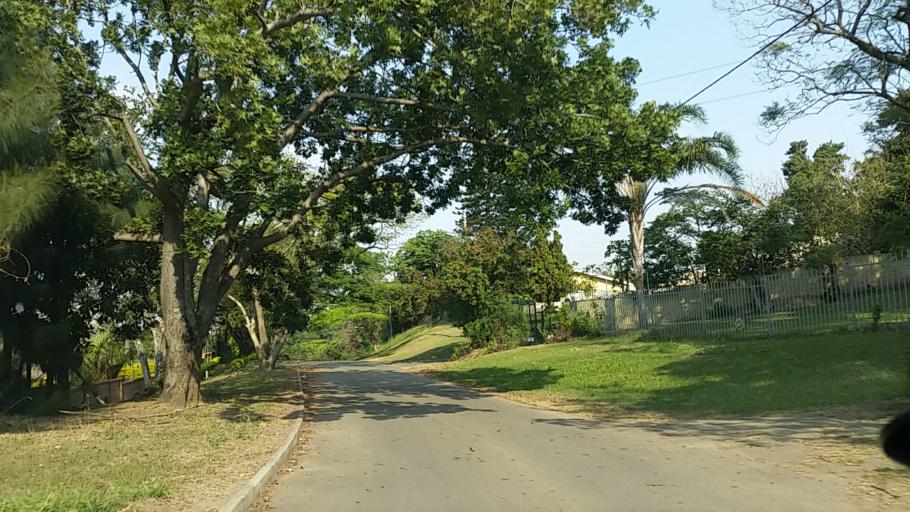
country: ZA
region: KwaZulu-Natal
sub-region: eThekwini Metropolitan Municipality
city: Berea
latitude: -29.8369
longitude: 30.9514
